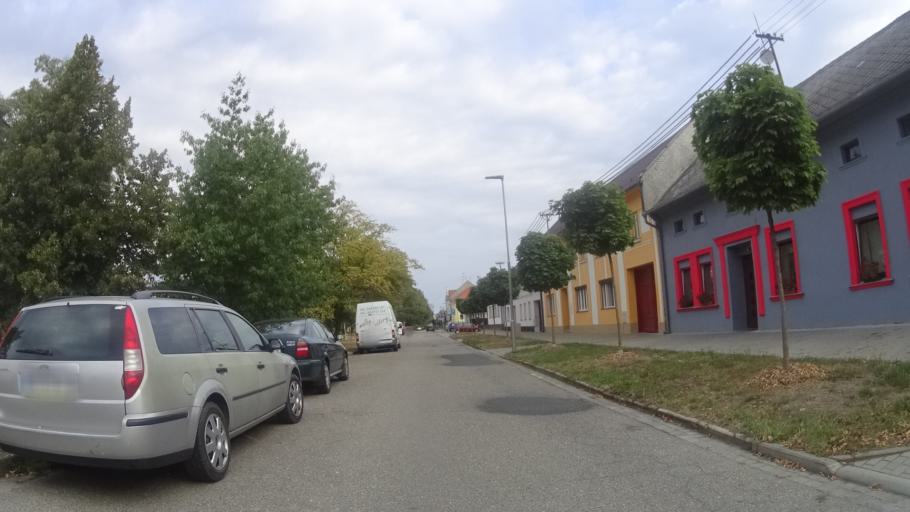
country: CZ
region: Zlin
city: Chropyne
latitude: 49.3569
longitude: 17.3646
